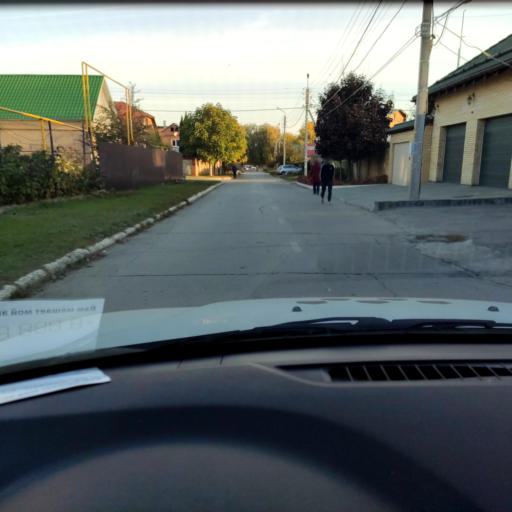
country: RU
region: Samara
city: Tol'yatti
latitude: 53.5250
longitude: 49.4217
